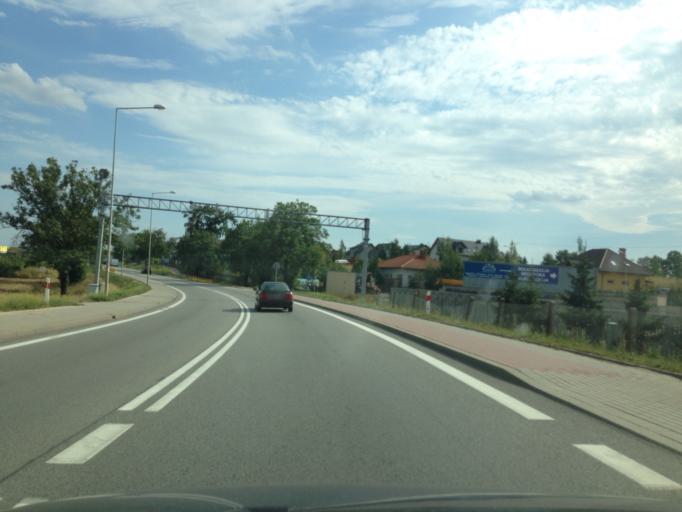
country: PL
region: Pomeranian Voivodeship
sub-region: Powiat gdanski
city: Pszczolki
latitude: 54.1824
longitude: 18.6797
